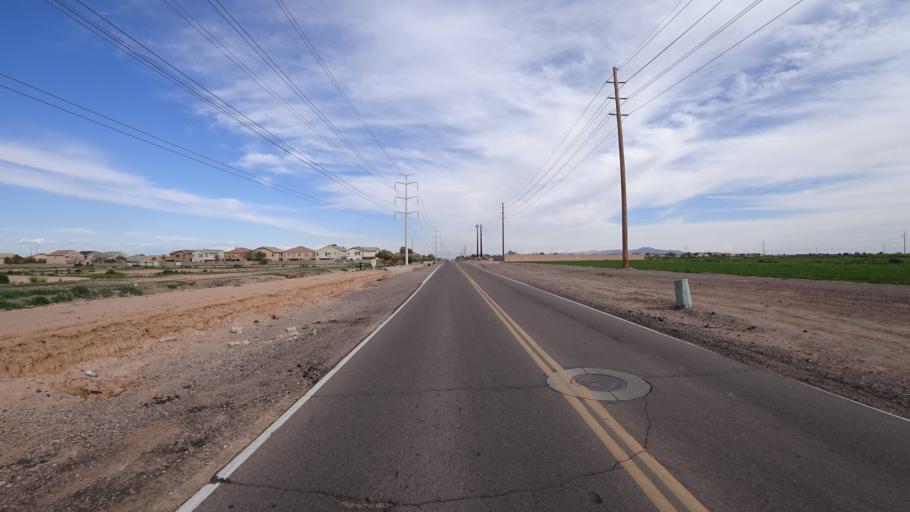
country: US
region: Arizona
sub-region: Maricopa County
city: Tolleson
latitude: 33.4065
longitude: -112.2865
